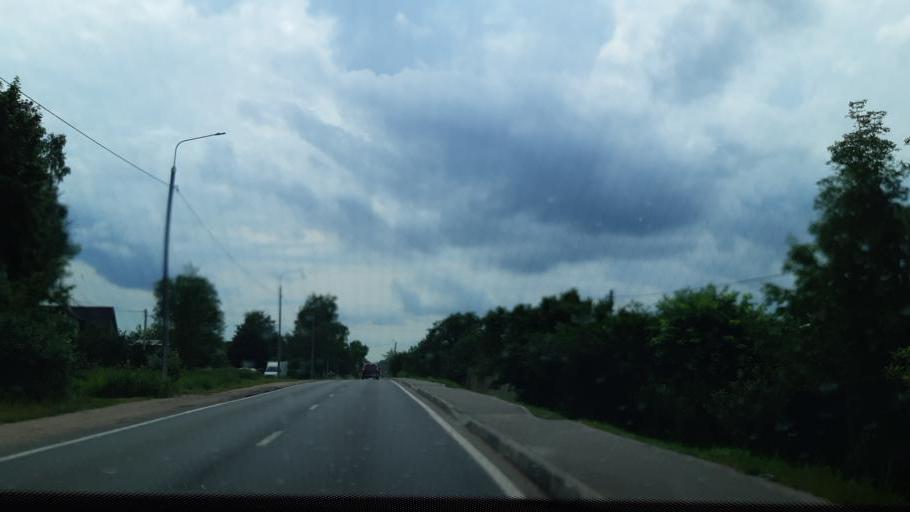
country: RU
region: Moskovskaya
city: Dorokhovo
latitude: 55.5370
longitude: 36.3637
